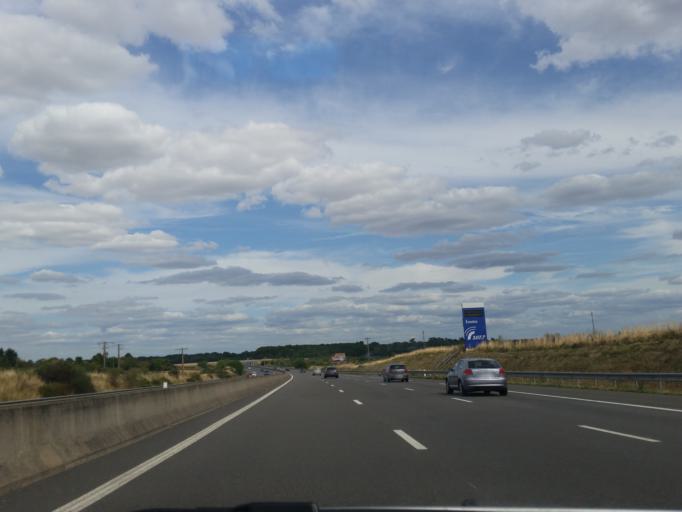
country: FR
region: Centre
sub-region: Departement du Loir-et-Cher
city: Saint-Sulpice-de-Pommeray
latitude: 47.6165
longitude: 1.2088
